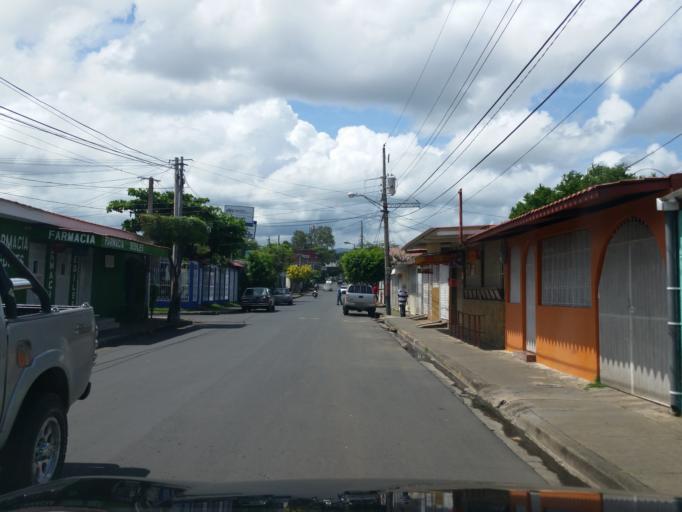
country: NI
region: Managua
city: Managua
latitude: 12.1283
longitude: -86.2402
